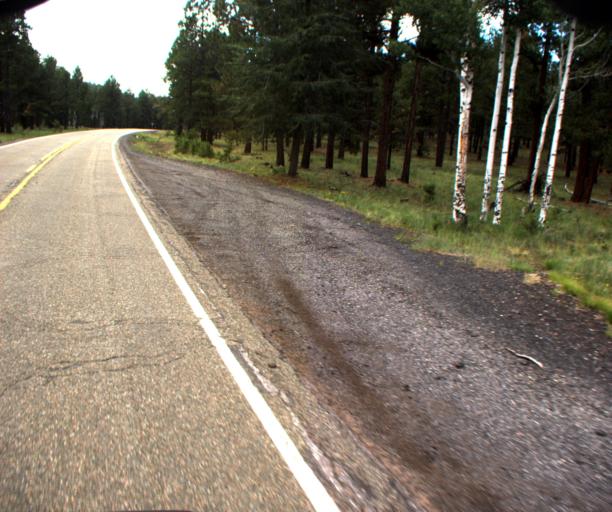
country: US
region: Arizona
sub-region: Coconino County
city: Parks
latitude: 35.3830
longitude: -111.7806
